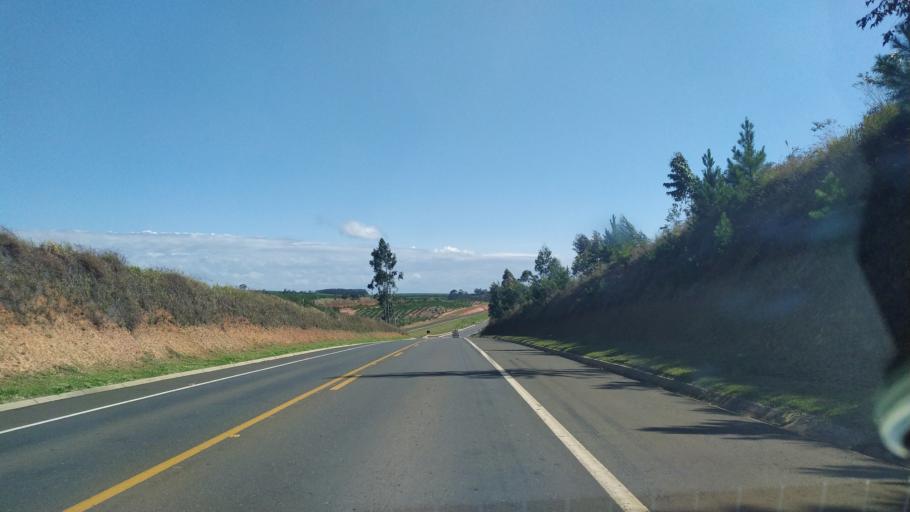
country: BR
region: Parana
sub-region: Ortigueira
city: Ortigueira
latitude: -24.2568
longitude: -50.7864
